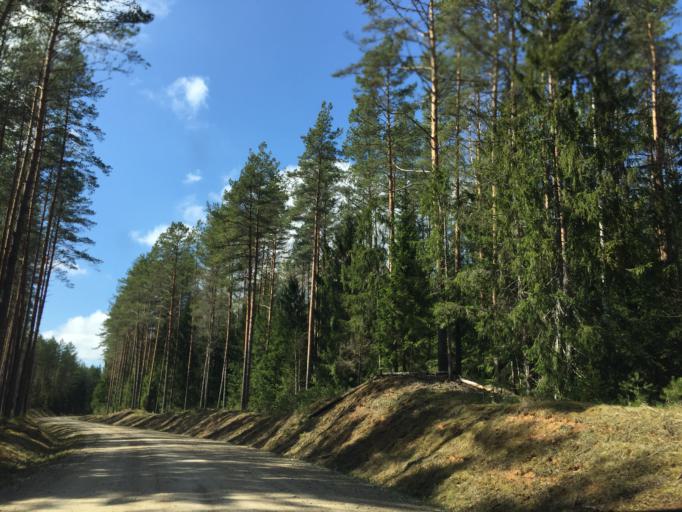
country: EE
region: Valgamaa
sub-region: Valga linn
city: Valga
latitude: 57.5948
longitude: 26.1300
